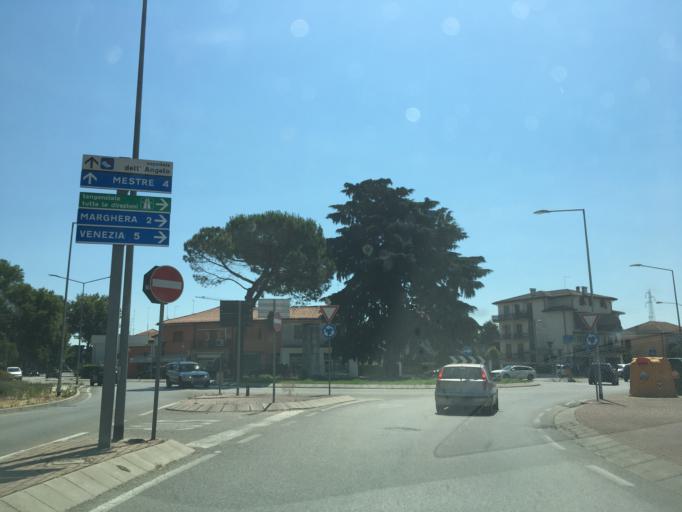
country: IT
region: Veneto
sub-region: Provincia di Venezia
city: Fornase
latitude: 45.4844
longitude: 12.1920
